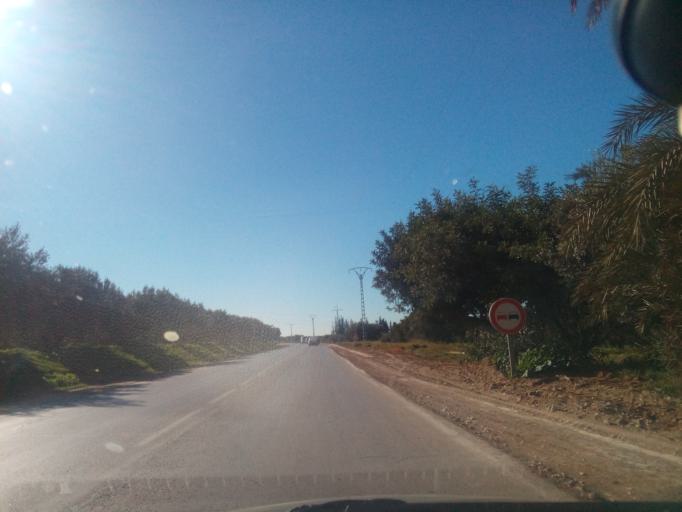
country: DZ
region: Relizane
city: Djidiouia
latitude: 35.9190
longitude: 0.7917
